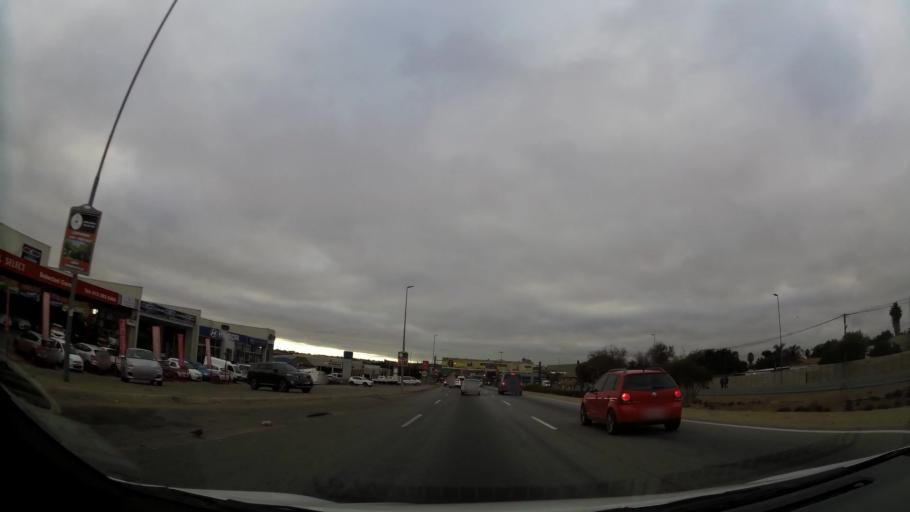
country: ZA
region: Limpopo
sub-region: Capricorn District Municipality
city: Polokwane
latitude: -23.9176
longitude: 29.4415
